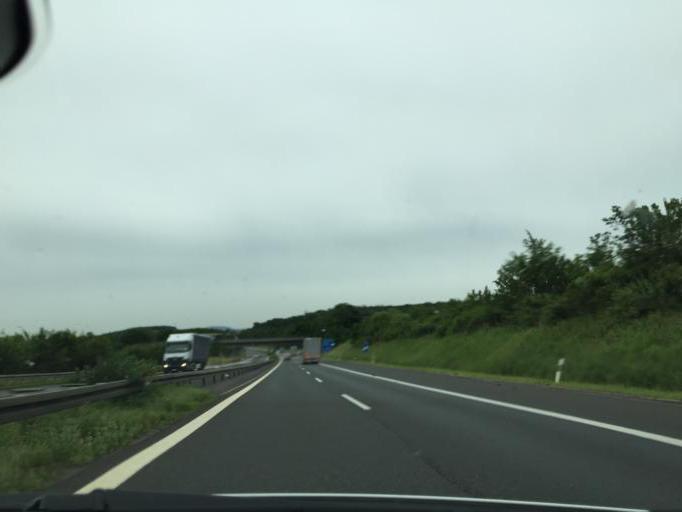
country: DE
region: Bavaria
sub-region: Regierungsbezirk Unterfranken
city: Schonungen
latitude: 50.0228
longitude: 10.3213
